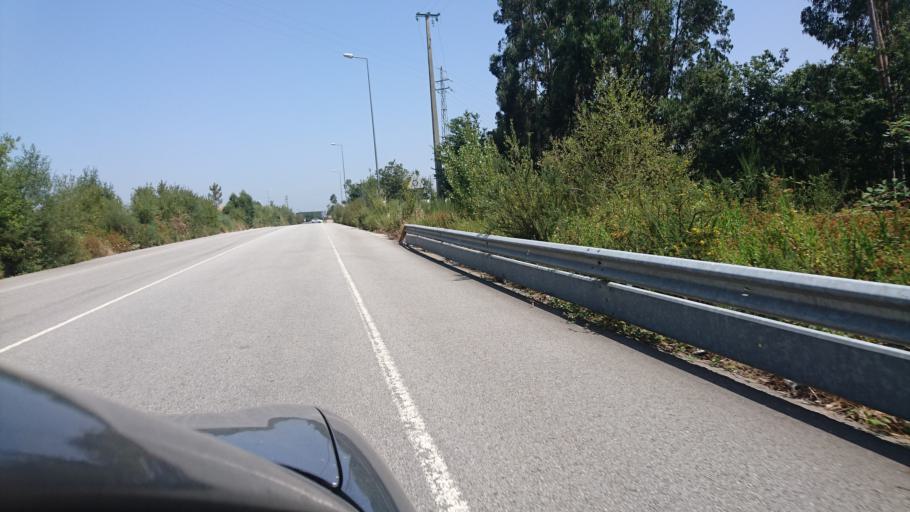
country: PT
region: Porto
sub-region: Valongo
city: Campo
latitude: 41.1693
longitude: -8.4406
